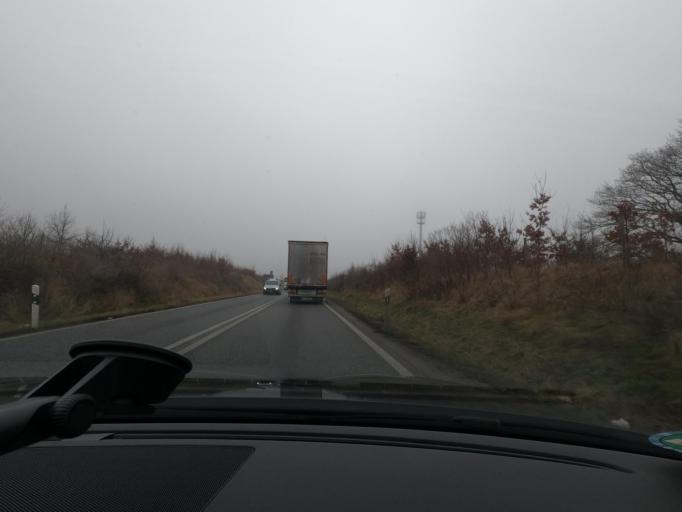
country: DE
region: North Rhine-Westphalia
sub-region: Regierungsbezirk Koln
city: Merzenich
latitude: 50.8443
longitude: 6.5183
